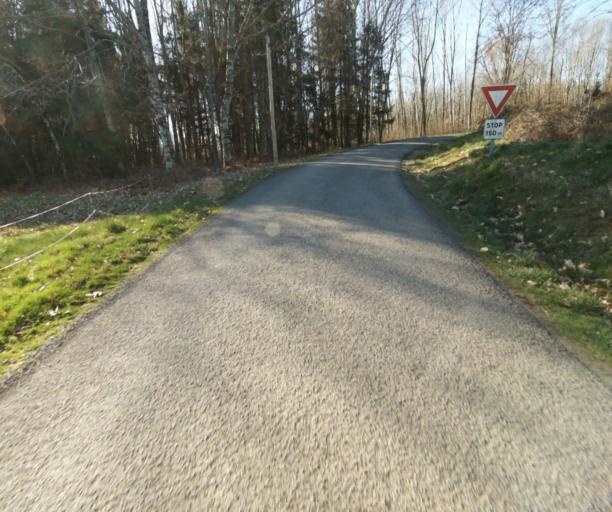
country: FR
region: Limousin
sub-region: Departement de la Correze
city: Seilhac
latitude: 45.3880
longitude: 1.7582
